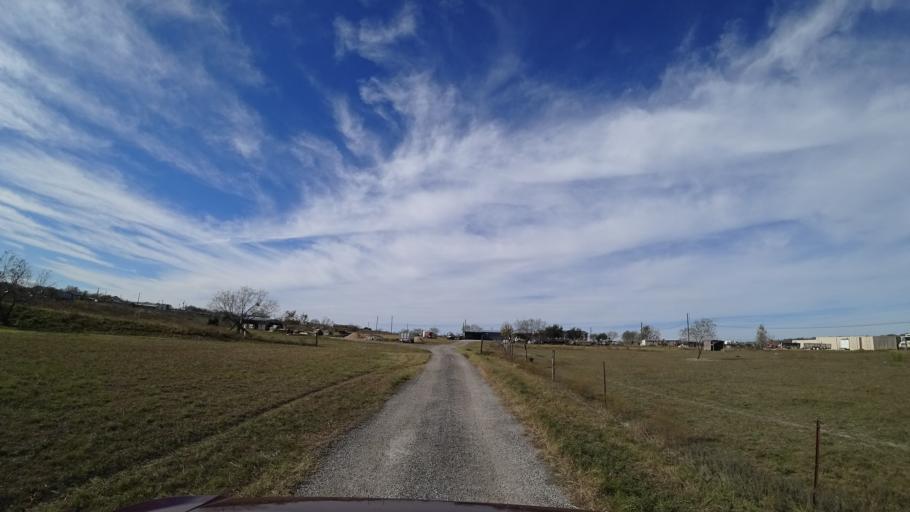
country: US
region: Texas
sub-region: Travis County
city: Onion Creek
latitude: 30.1184
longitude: -97.7182
